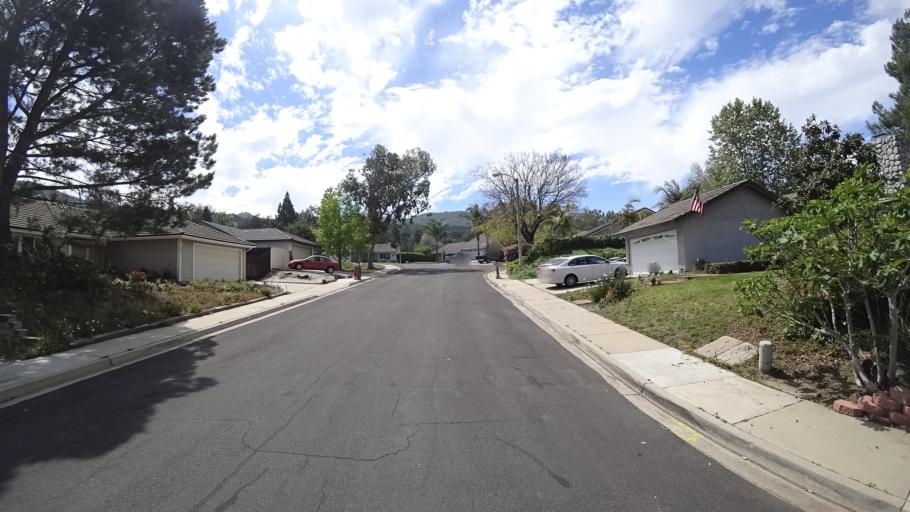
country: US
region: California
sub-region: Ventura County
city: Casa Conejo
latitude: 34.1622
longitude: -118.9430
